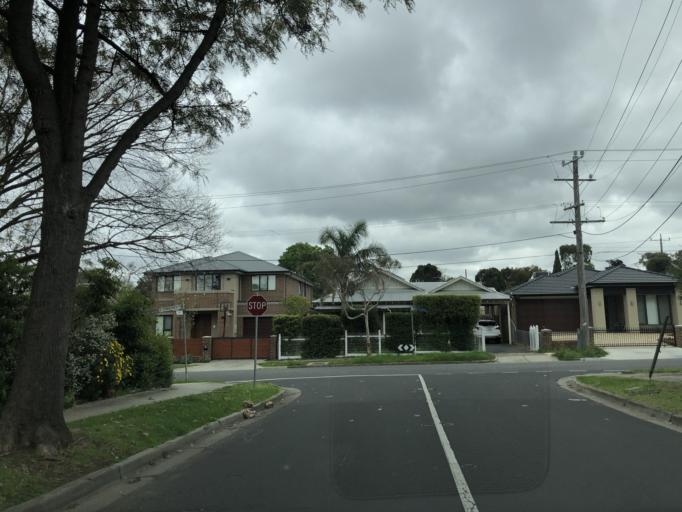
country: AU
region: Victoria
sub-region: Whitehorse
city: Blackburn South
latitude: -37.8372
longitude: 145.1402
